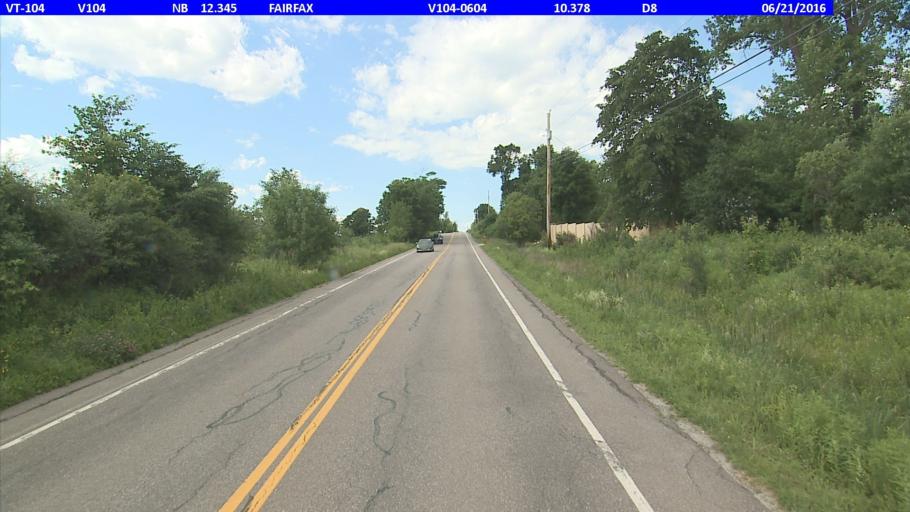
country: US
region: Vermont
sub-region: Franklin County
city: Saint Albans
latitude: 44.7335
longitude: -73.0475
